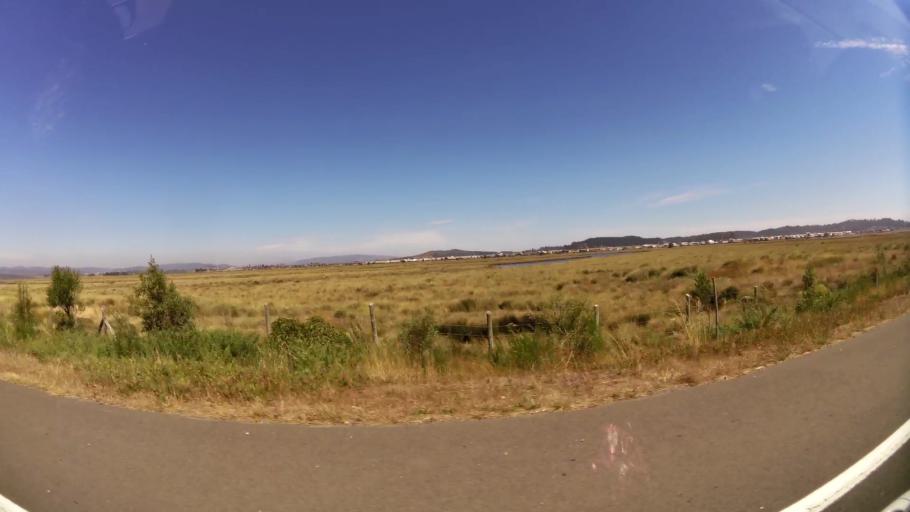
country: CL
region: Biobio
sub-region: Provincia de Concepcion
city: Talcahuano
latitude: -36.7338
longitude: -73.0828
